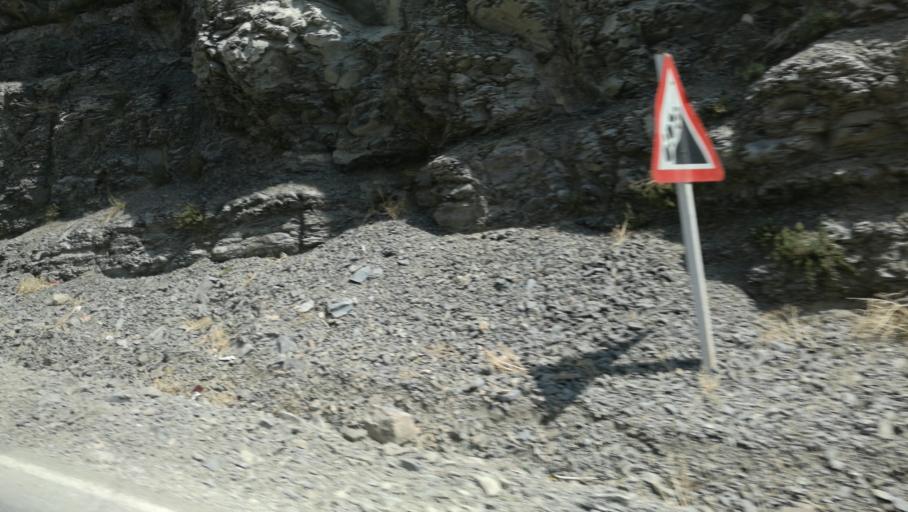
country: IR
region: Alborz
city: Karaj
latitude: 35.9399
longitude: 51.0749
